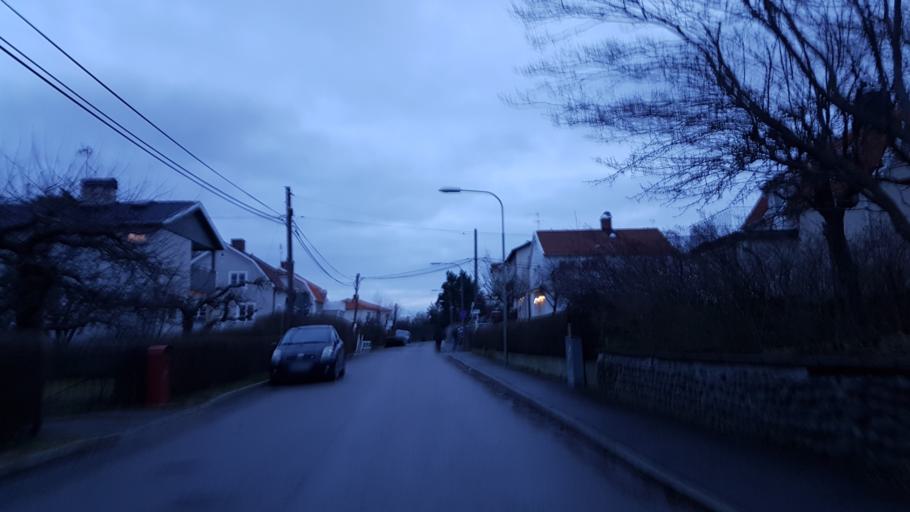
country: SE
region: Stockholm
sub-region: Stockholms Kommun
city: Arsta
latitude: 59.2785
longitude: 18.0502
